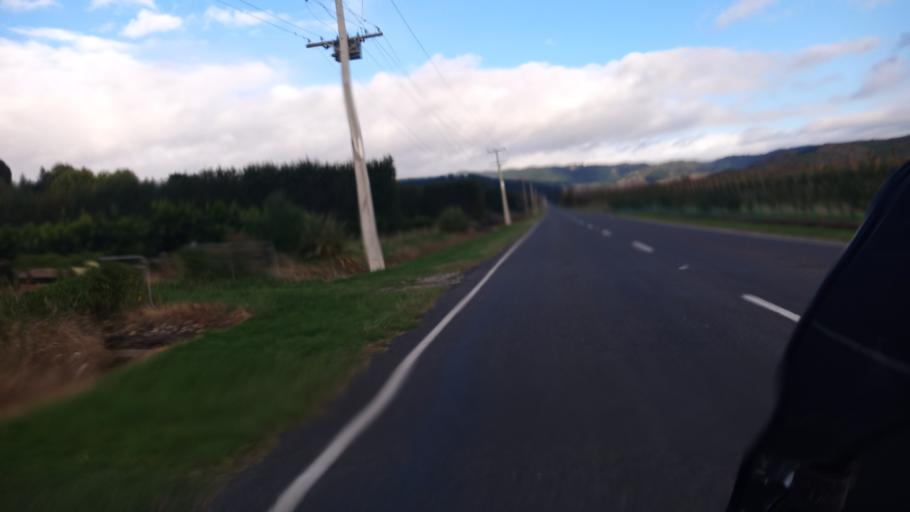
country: NZ
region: Gisborne
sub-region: Gisborne District
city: Gisborne
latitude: -38.6323
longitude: 177.8780
